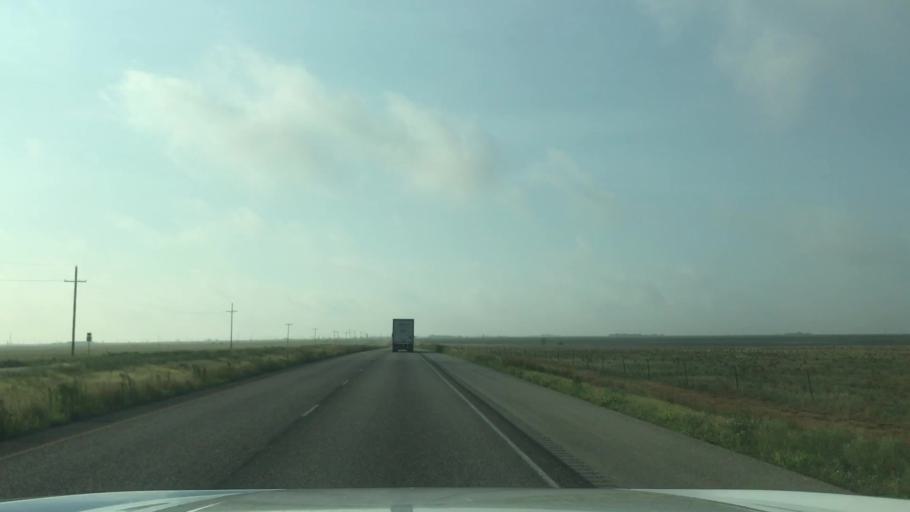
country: US
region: Texas
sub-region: Garza County
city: Post
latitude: 33.2533
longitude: -101.4683
